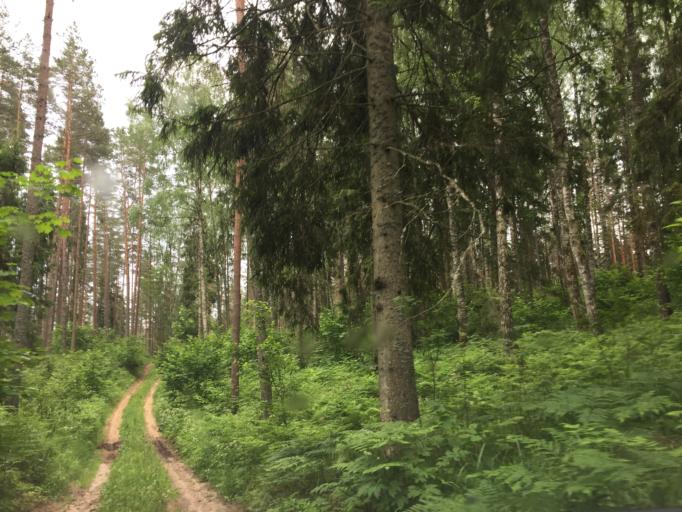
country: LV
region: Tukuma Rajons
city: Tukums
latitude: 57.0293
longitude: 23.0765
